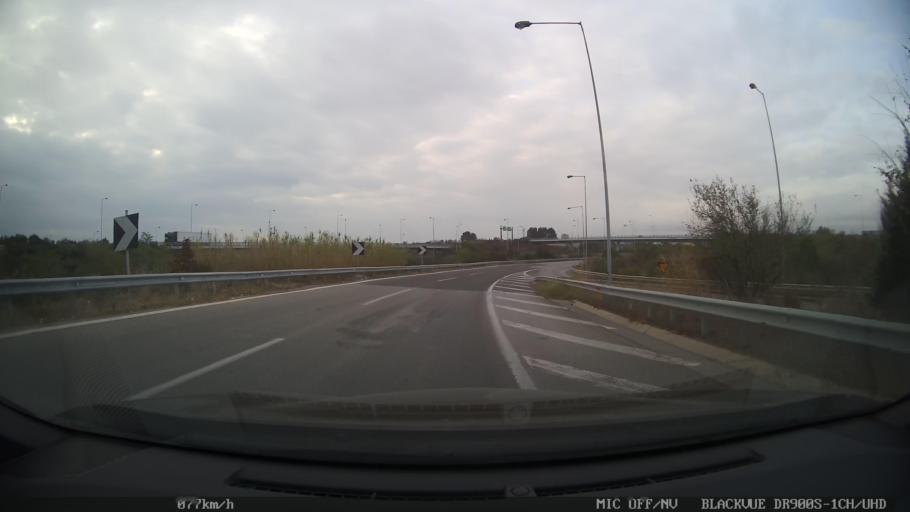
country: GR
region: Central Macedonia
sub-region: Nomos Thessalonikis
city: Kalochori
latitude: 40.6548
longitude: 22.8423
